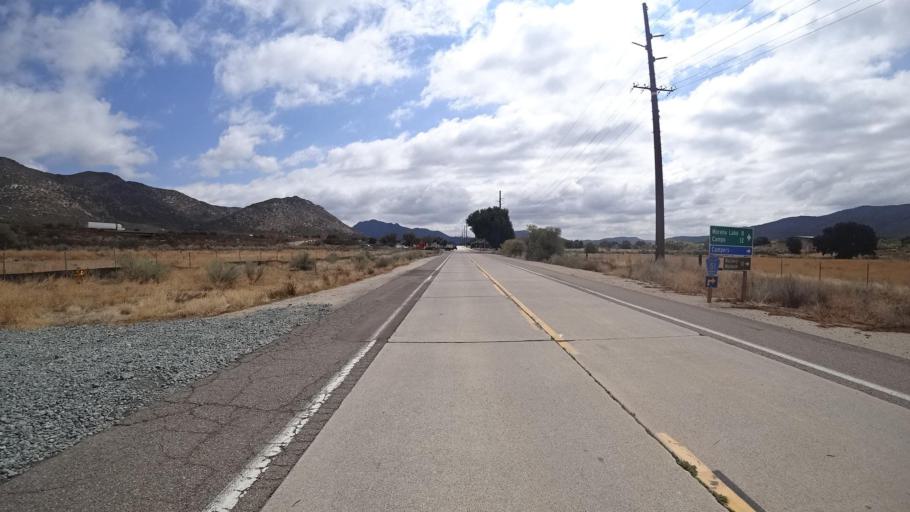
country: US
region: California
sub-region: San Diego County
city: Pine Valley
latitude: 32.7609
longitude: -116.4881
